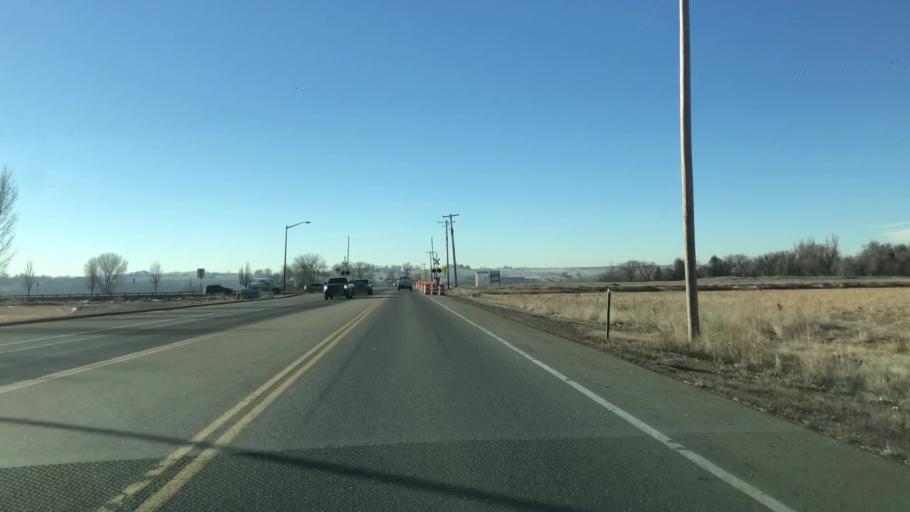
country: US
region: Colorado
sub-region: Larimer County
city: Loveland
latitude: 40.4011
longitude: -105.0212
